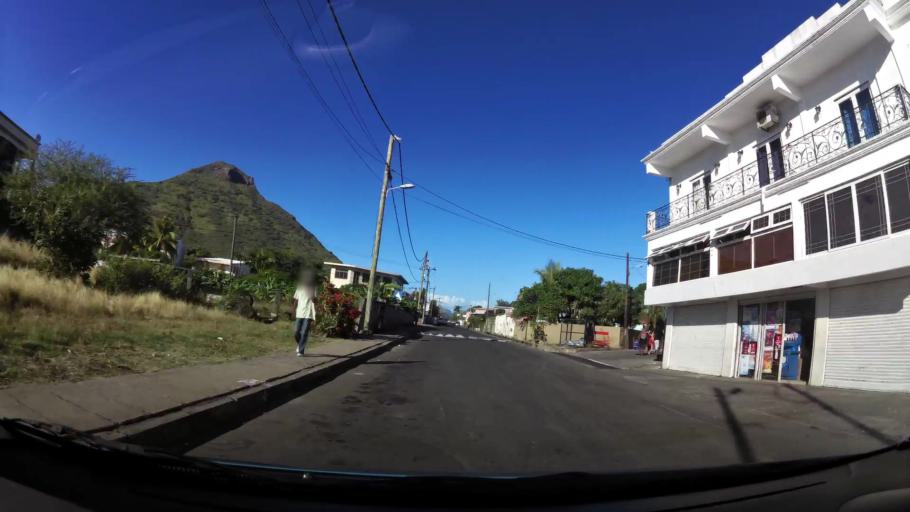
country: MU
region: Black River
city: Tamarin
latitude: -20.3310
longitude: 57.3729
